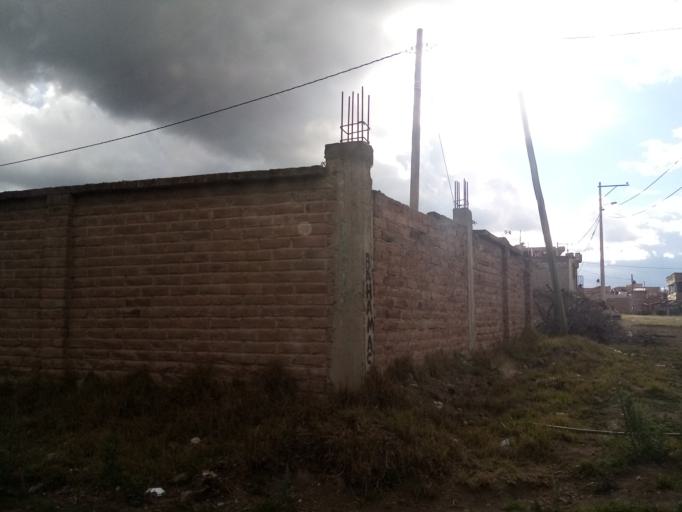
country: EC
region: Chimborazo
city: Riobamba
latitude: -1.6859
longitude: -78.6264
